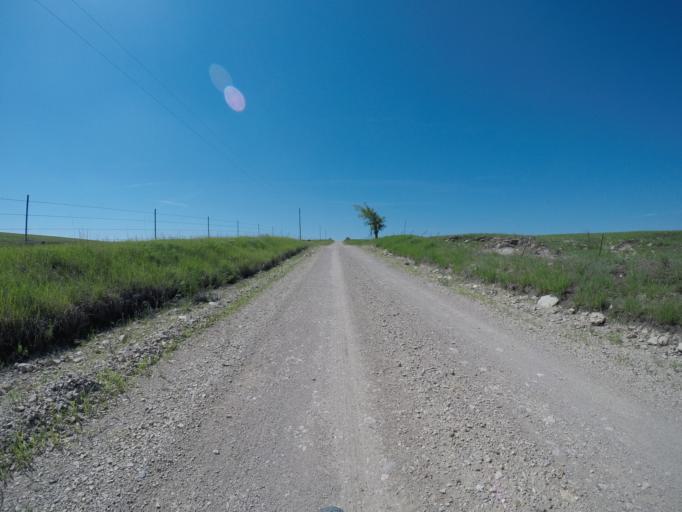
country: US
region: Kansas
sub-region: Wabaunsee County
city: Alma
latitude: 39.0039
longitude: -96.1783
